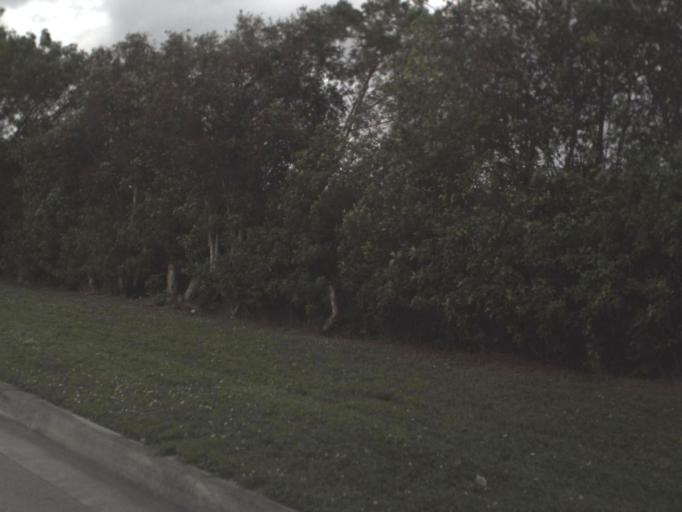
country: US
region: Florida
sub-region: Miami-Dade County
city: Doral
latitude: 25.8118
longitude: -80.3746
